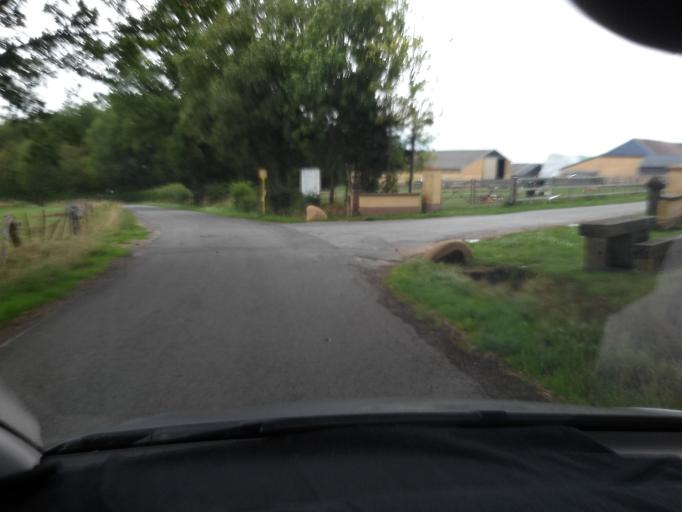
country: BE
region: Wallonia
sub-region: Province du Luxembourg
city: Attert
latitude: 49.7455
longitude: 5.8125
